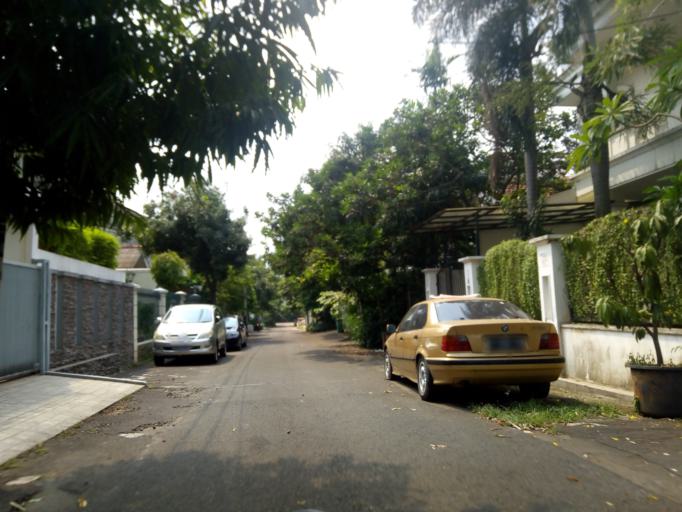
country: ID
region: Jakarta Raya
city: Jakarta
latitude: -6.2367
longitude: 106.7907
